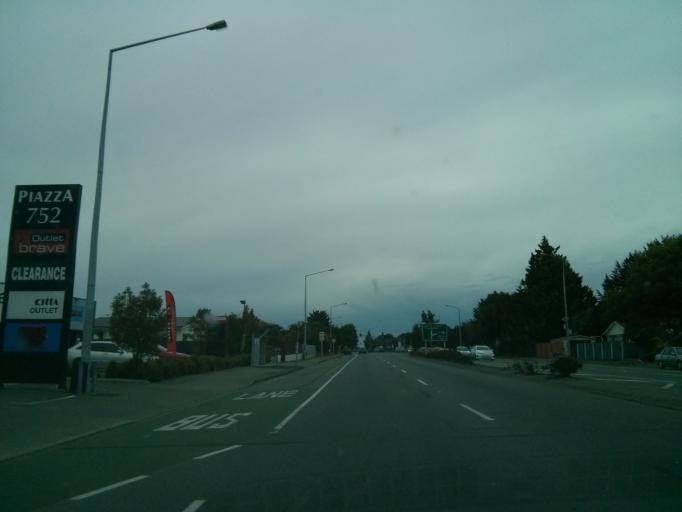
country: NZ
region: Canterbury
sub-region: Waimakariri District
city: Kaiapoi
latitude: -43.4490
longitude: 172.6299
